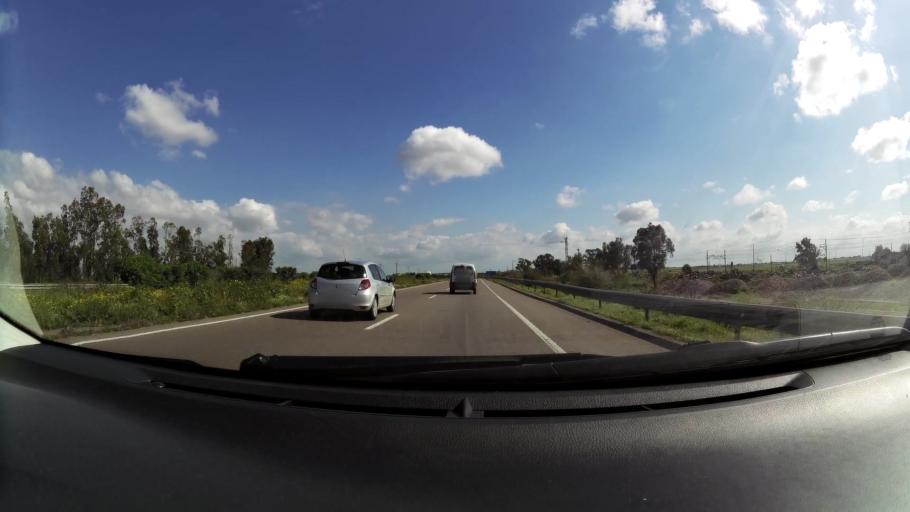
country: MA
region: Chaouia-Ouardigha
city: Nouaseur
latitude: 33.3638
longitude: -7.6198
